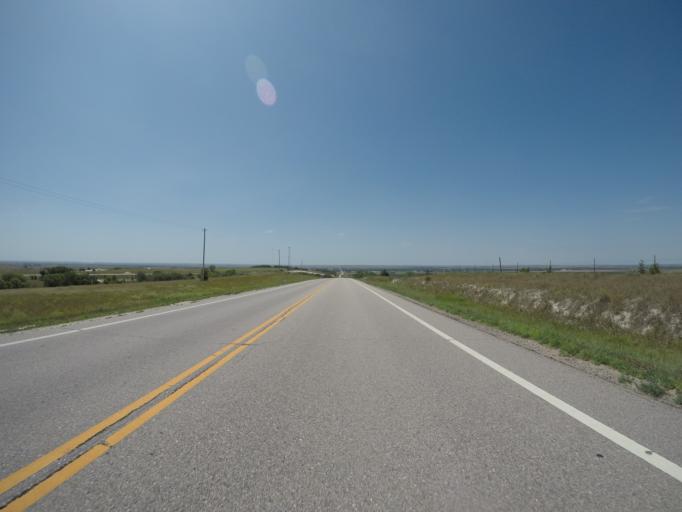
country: US
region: Kansas
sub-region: Osborne County
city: Osborne
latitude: 39.4750
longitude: -98.6943
